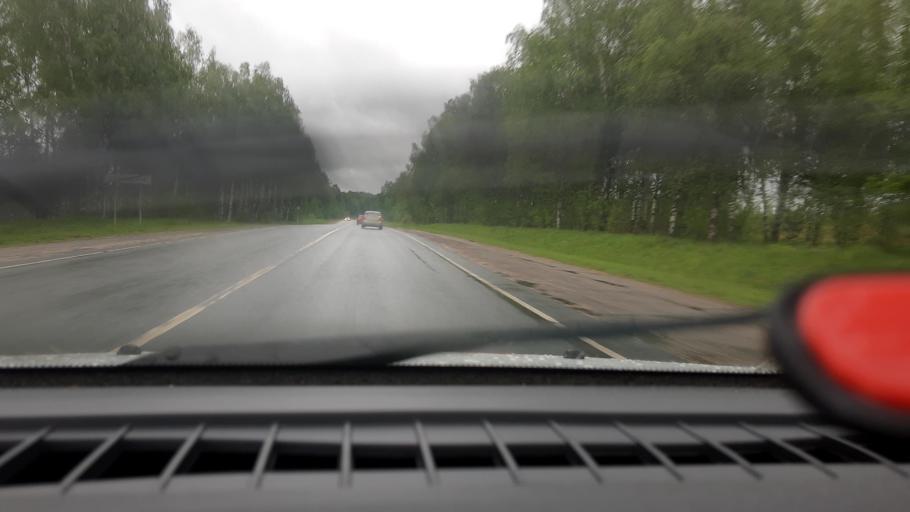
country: RU
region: Nizjnij Novgorod
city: Linda
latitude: 56.6192
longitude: 44.0722
